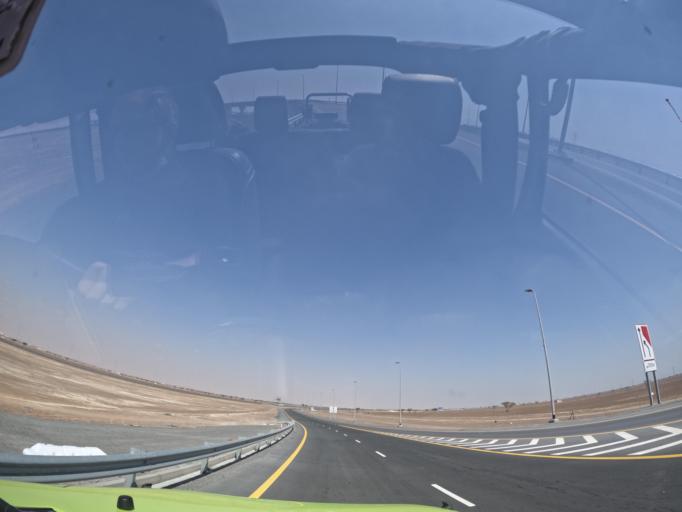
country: AE
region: Ash Shariqah
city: Adh Dhayd
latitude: 24.9113
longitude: 55.8037
